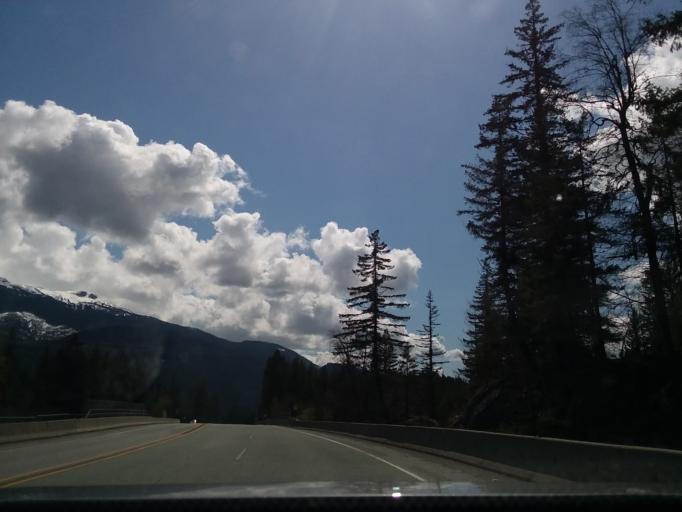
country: CA
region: British Columbia
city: Whistler
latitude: 50.0338
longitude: -123.1235
